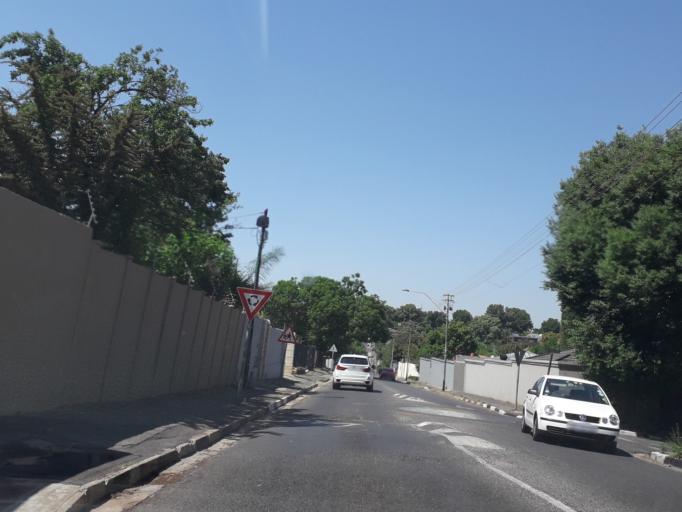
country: ZA
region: Gauteng
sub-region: City of Johannesburg Metropolitan Municipality
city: Johannesburg
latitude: -26.1369
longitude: 28.0243
